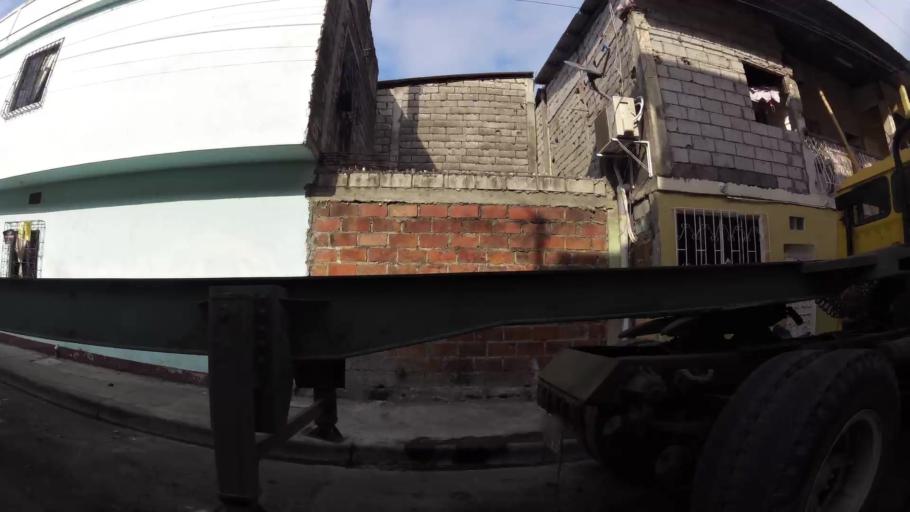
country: EC
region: Guayas
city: Guayaquil
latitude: -2.2503
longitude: -79.9051
